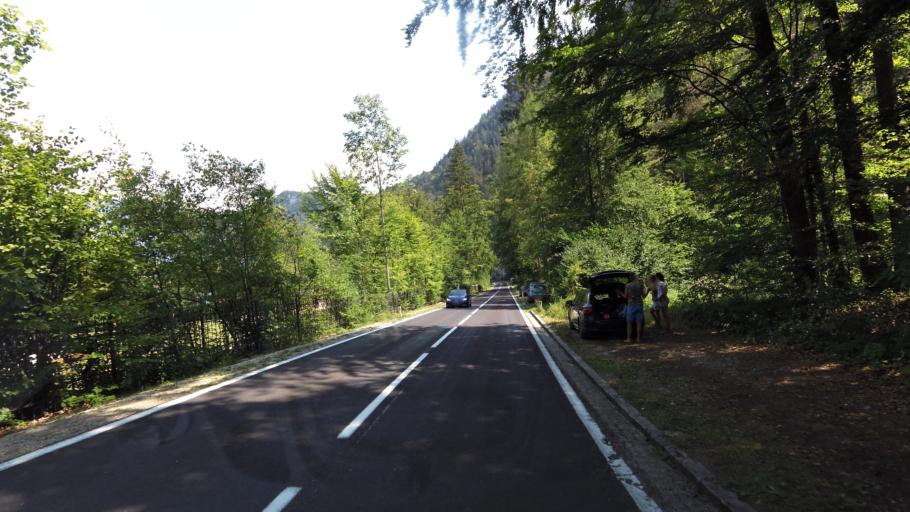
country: AT
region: Upper Austria
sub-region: Politischer Bezirk Vocklabruck
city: Steinbach am Attersee
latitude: 47.7899
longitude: 13.4956
